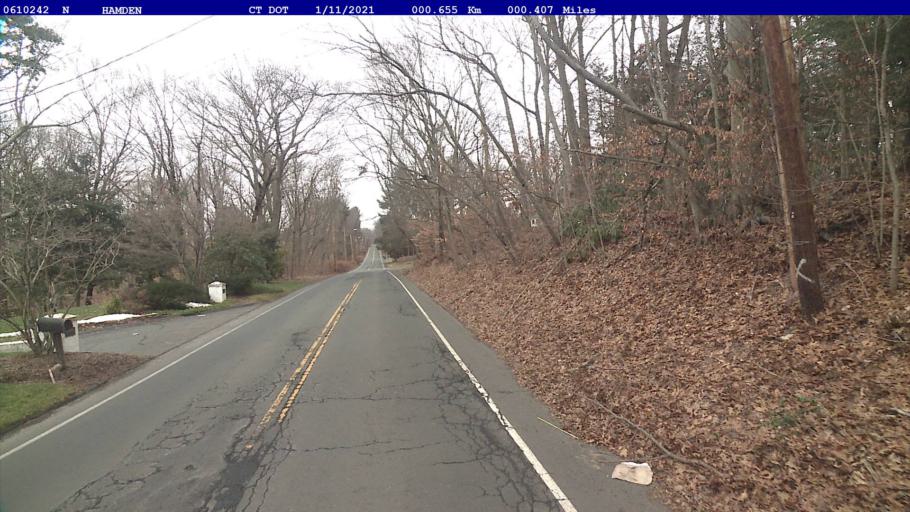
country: US
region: Connecticut
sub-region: New Haven County
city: New Haven
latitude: 41.3442
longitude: -72.9058
